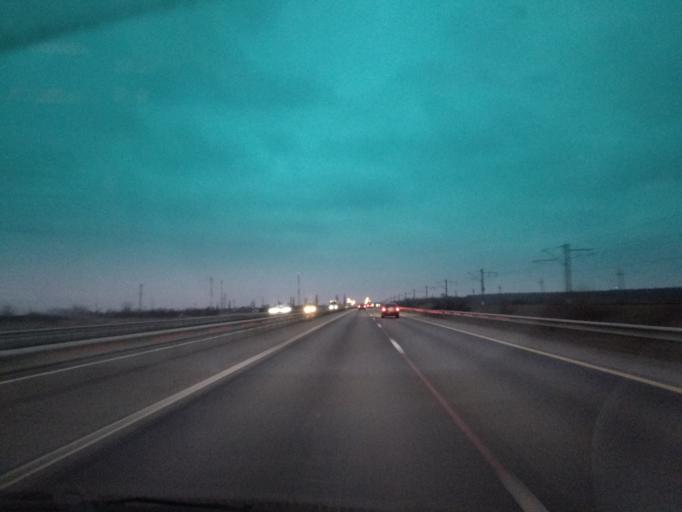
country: RU
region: Adygeya
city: Adygeysk
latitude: 44.8123
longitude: 39.2280
